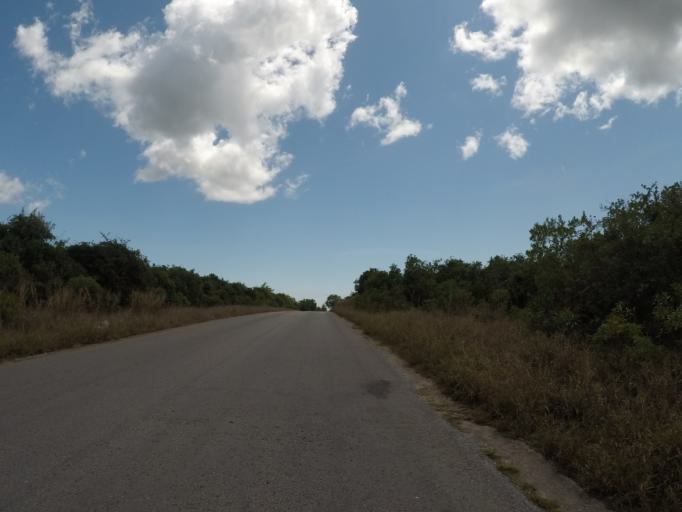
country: TZ
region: Zanzibar Central/South
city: Nganane
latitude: -6.2812
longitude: 39.4740
